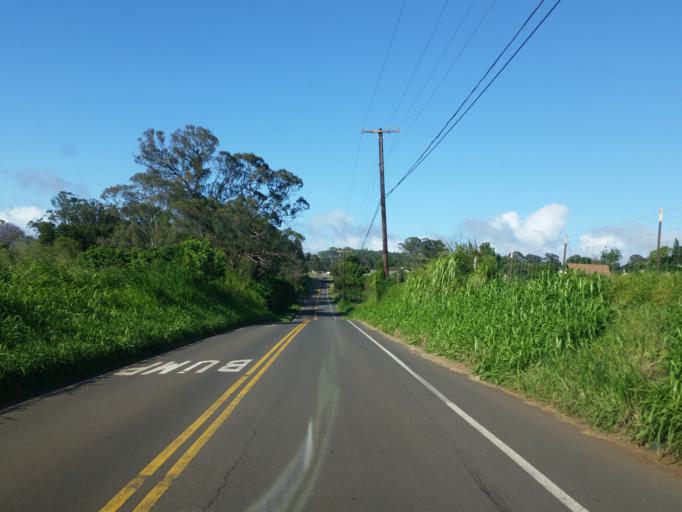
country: US
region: Hawaii
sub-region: Maui County
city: Makawao
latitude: 20.8378
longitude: -156.3096
